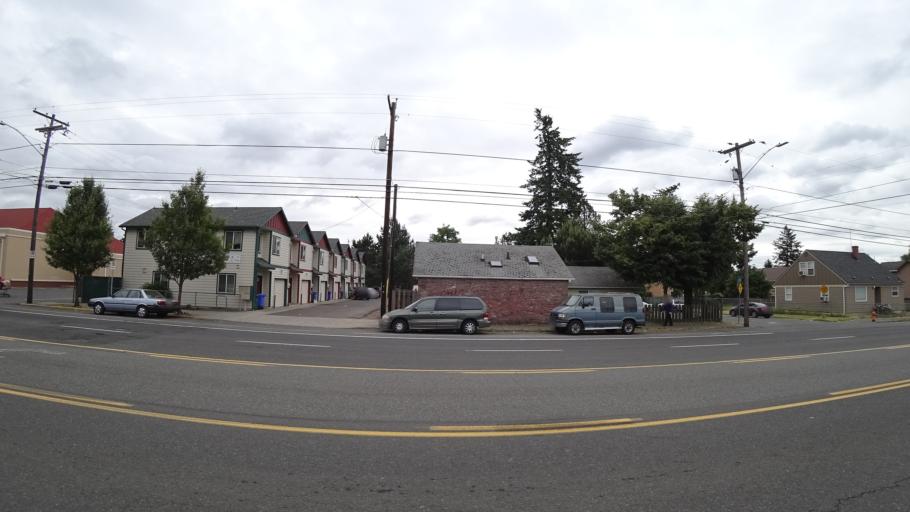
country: US
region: Oregon
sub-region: Multnomah County
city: Lents
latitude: 45.5003
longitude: -122.5378
